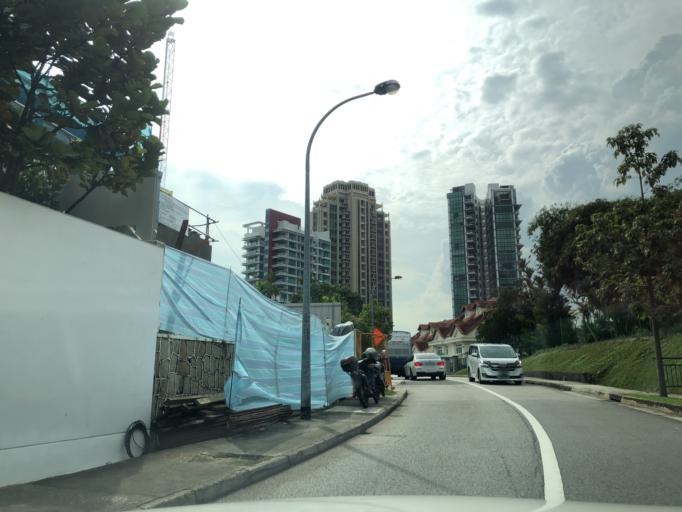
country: SG
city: Singapore
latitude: 1.3016
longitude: 103.8264
